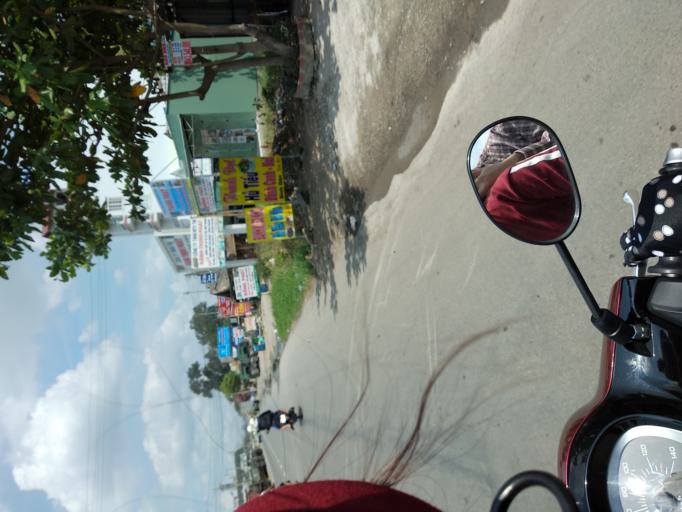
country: VN
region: Dong Nai
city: Long Thanh
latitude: 10.7390
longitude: 106.9519
